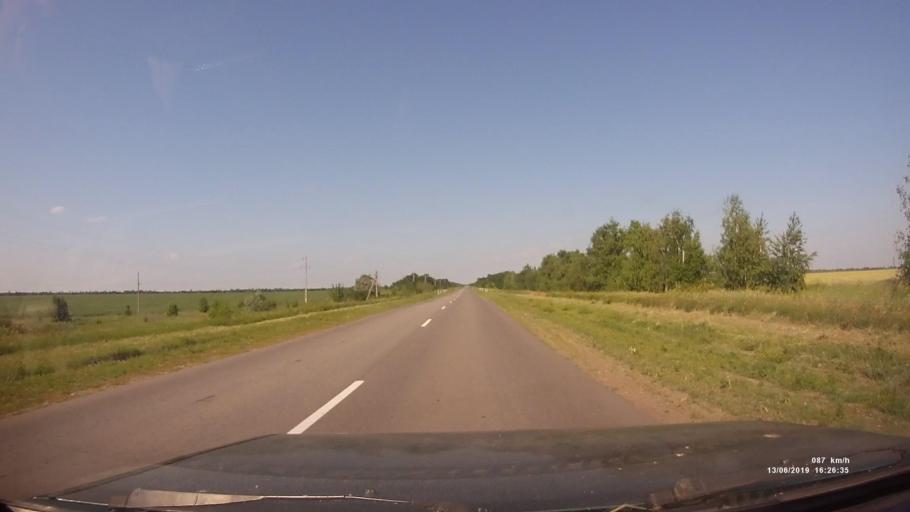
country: RU
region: Rostov
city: Kazanskaya
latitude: 49.8061
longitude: 41.1680
